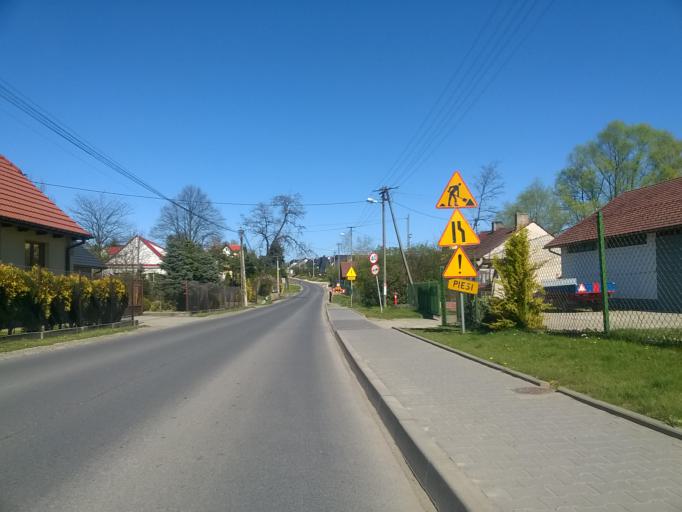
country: PL
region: Lesser Poland Voivodeship
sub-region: Powiat krakowski
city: Michalowice
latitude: 50.1084
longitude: 19.9878
